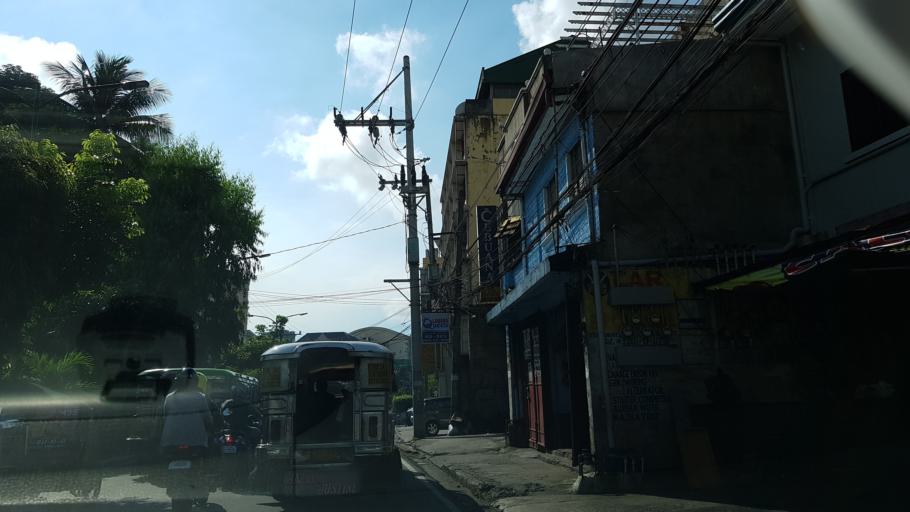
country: PH
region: Metro Manila
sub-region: Mandaluyong
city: Mandaluyong City
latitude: 14.5736
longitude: 121.0448
